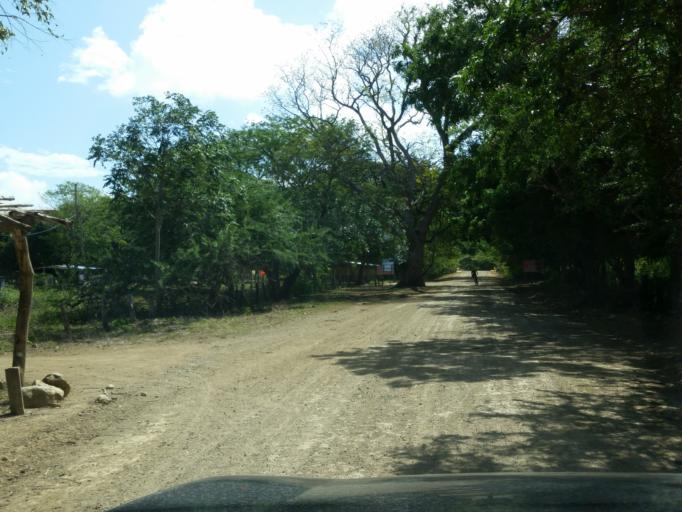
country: NI
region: Rivas
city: San Juan del Sur
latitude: 11.1403
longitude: -85.7847
